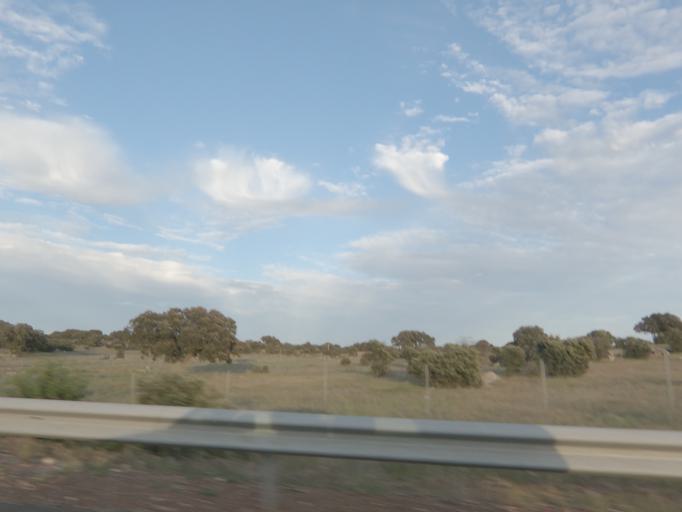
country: ES
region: Extremadura
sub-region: Provincia de Badajoz
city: Mirandilla
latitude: 38.9852
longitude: -6.3320
